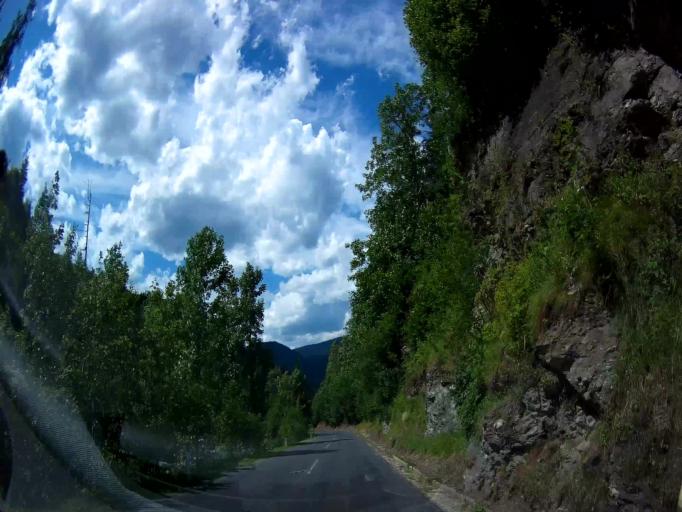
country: AT
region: Styria
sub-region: Politischer Bezirk Murau
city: Stadl an der Mur
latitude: 47.0658
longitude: 13.9870
